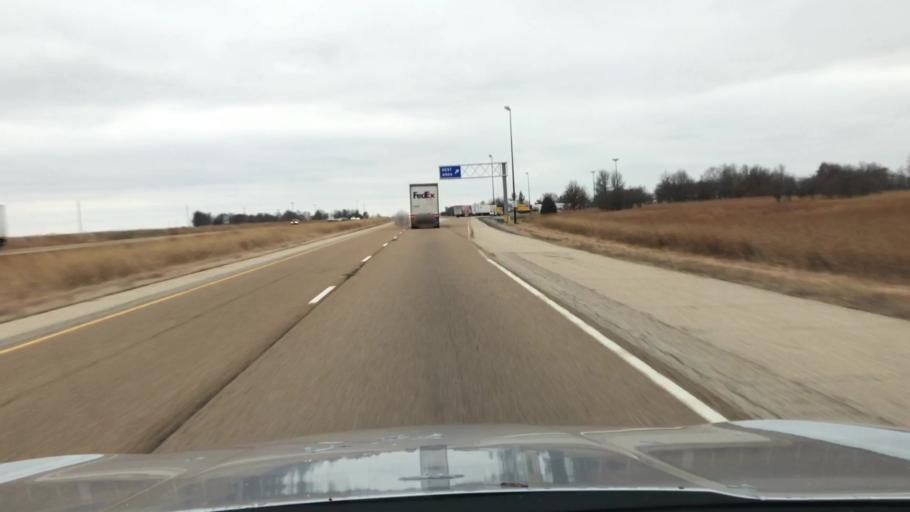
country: US
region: Illinois
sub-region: Montgomery County
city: Raymond
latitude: 39.3565
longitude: -89.6430
